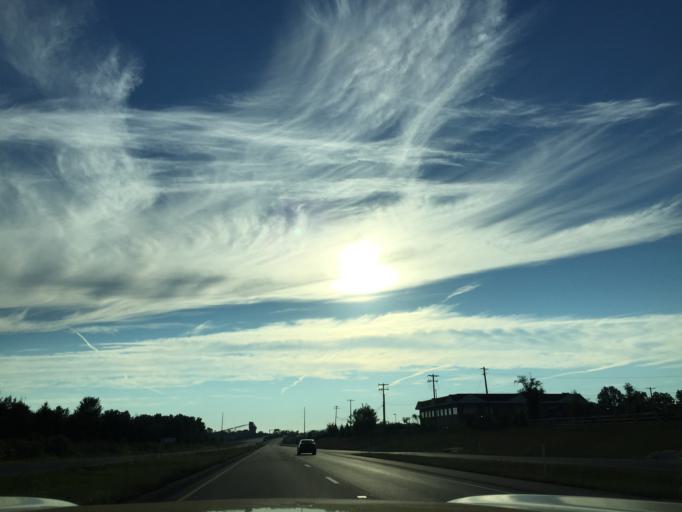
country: US
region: Pennsylvania
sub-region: Lehigh County
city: Wescosville
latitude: 40.5678
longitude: -75.5599
